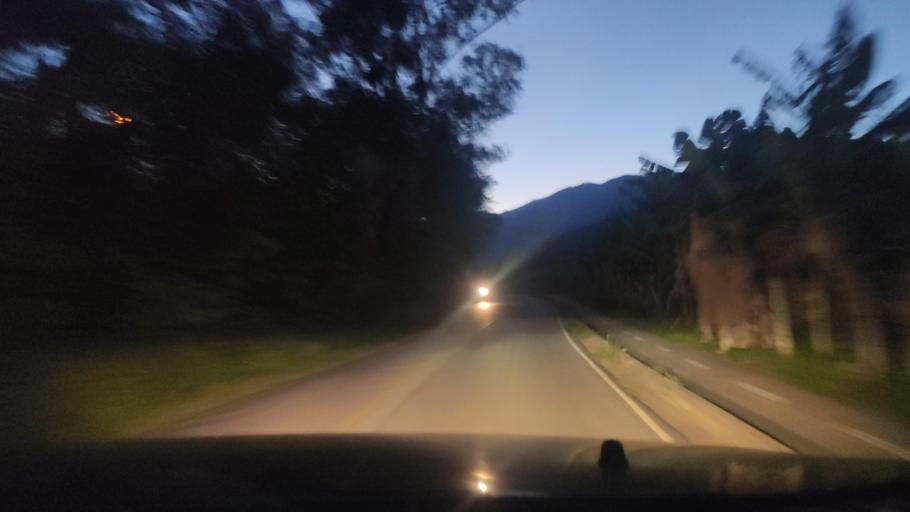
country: BR
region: Minas Gerais
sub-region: Paraisopolis
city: Paraisopolis
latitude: -22.7040
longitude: -45.7604
